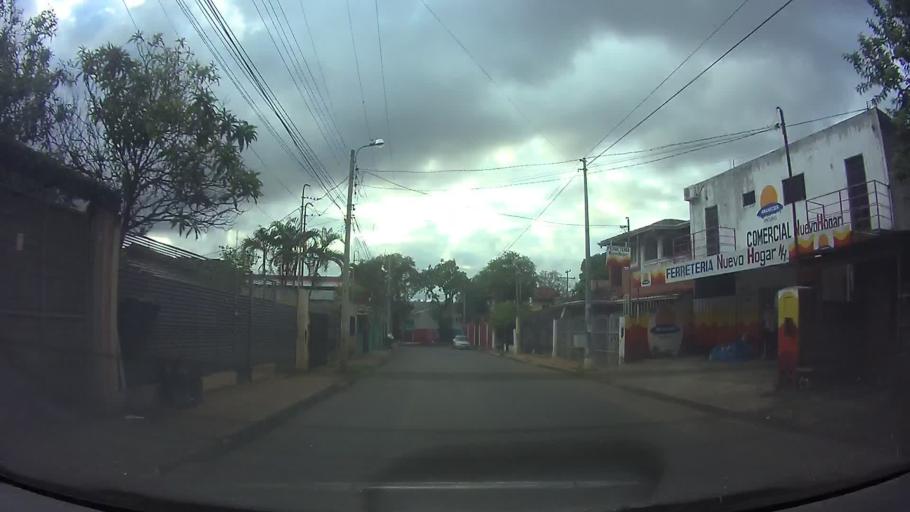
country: PY
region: Central
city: Fernando de la Mora
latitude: -25.3134
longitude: -57.5528
